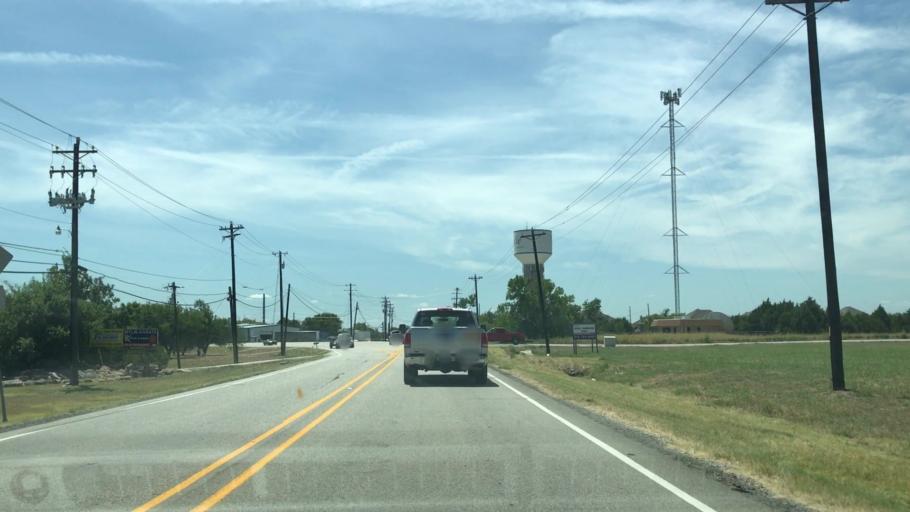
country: US
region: Texas
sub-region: Collin County
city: Saint Paul
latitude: 33.0309
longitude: -96.5471
